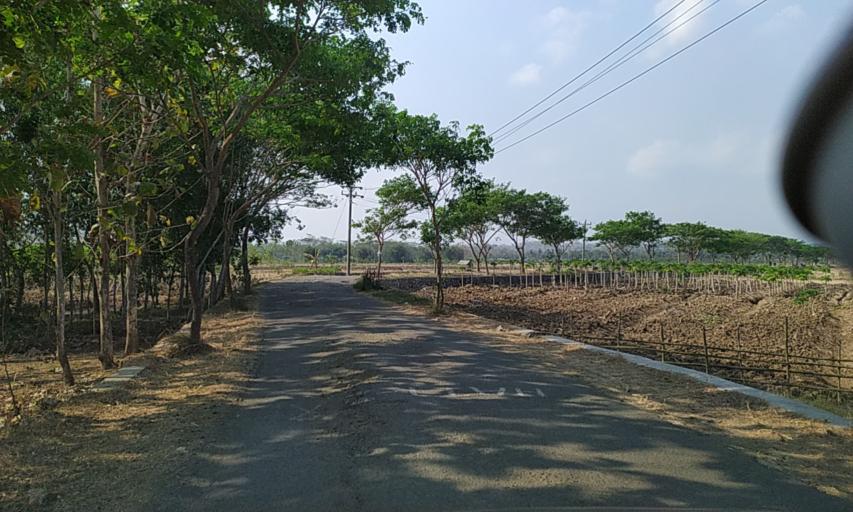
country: ID
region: Central Java
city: Muktisari
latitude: -7.5014
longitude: 108.8858
